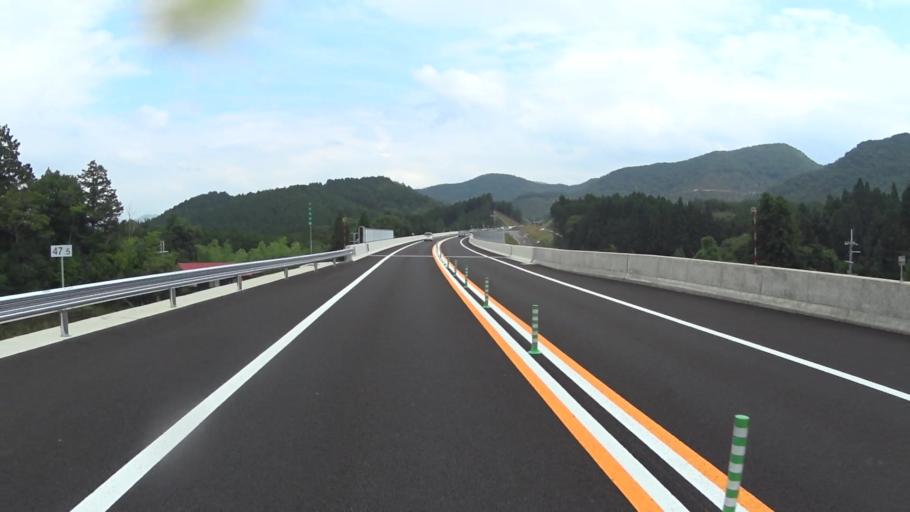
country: JP
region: Kyoto
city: Ayabe
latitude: 35.1669
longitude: 135.3822
